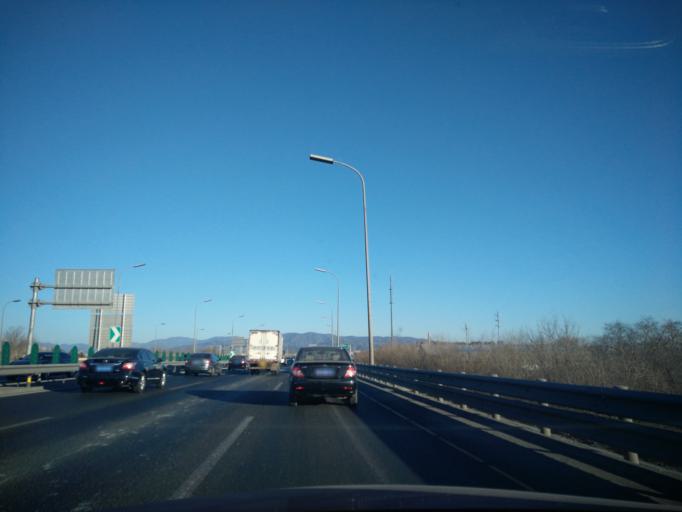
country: CN
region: Beijing
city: Lugu
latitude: 39.8706
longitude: 116.2038
